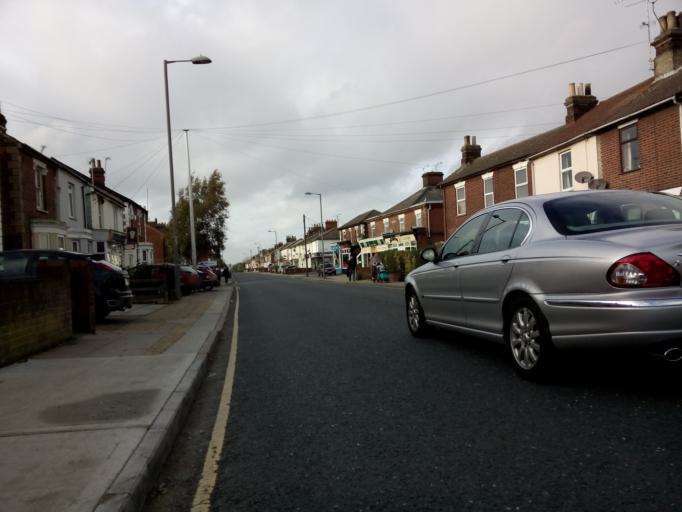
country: GB
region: England
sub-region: Suffolk
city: Ipswich
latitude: 52.0483
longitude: 1.1795
